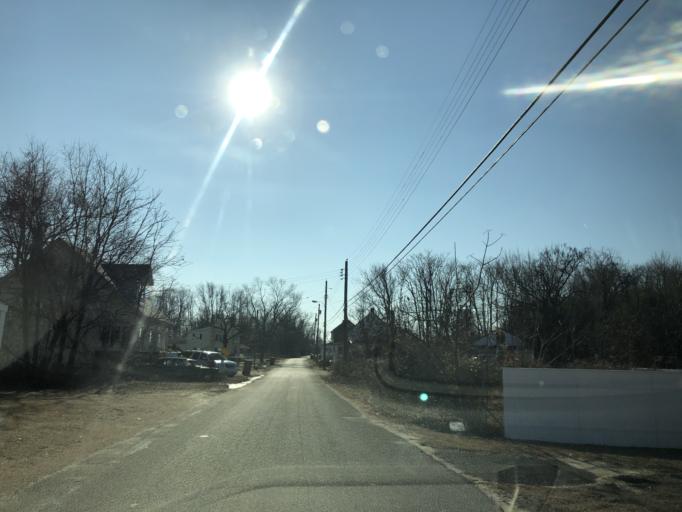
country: US
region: New Jersey
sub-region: Gloucester County
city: Beckett
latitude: 39.7966
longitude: -75.3537
